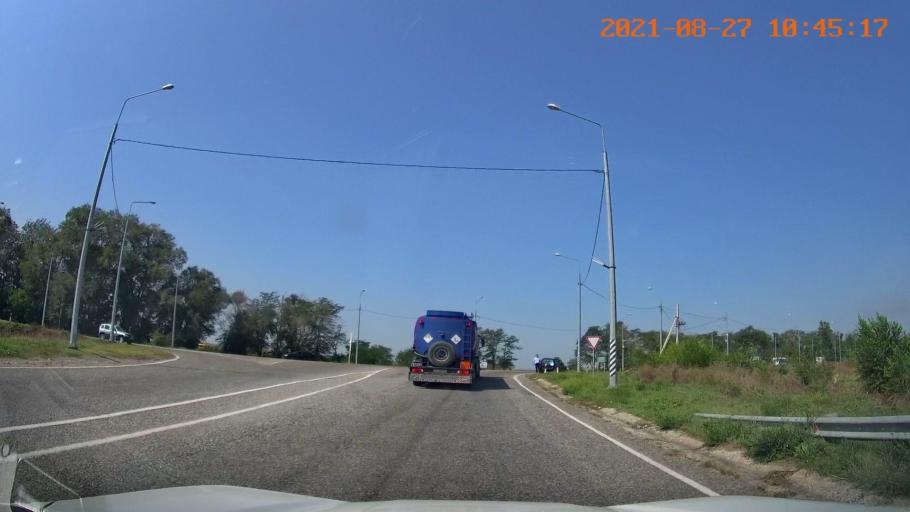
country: RU
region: Karachayevo-Cherkesiya
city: Psyzh
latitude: 44.3011
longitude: 42.0039
